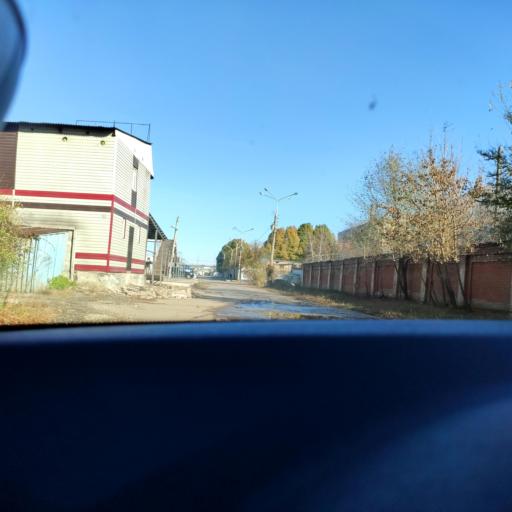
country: RU
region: Samara
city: Samara
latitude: 53.2099
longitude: 50.2638
